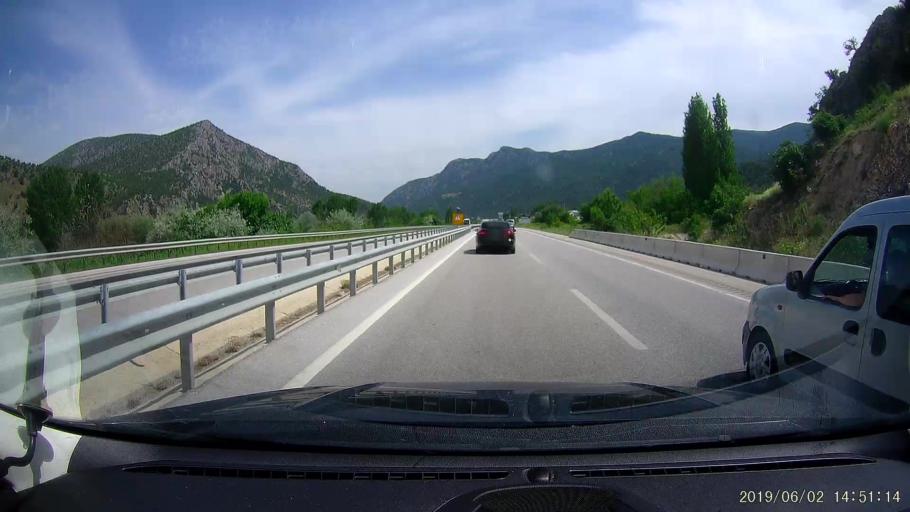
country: TR
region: Corum
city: Kargi
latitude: 41.0633
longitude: 34.5373
